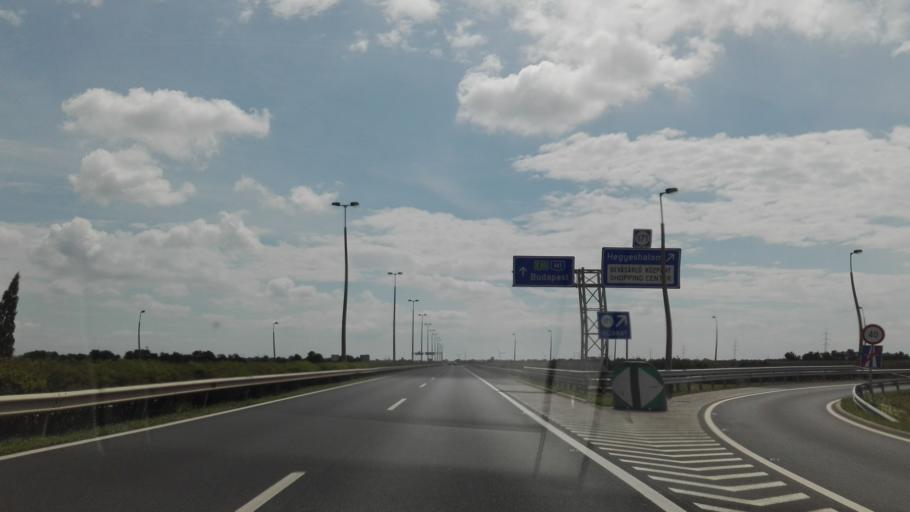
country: AT
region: Burgenland
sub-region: Politischer Bezirk Neusiedl am See
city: Nickelsdorf
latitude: 47.9158
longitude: 17.1245
